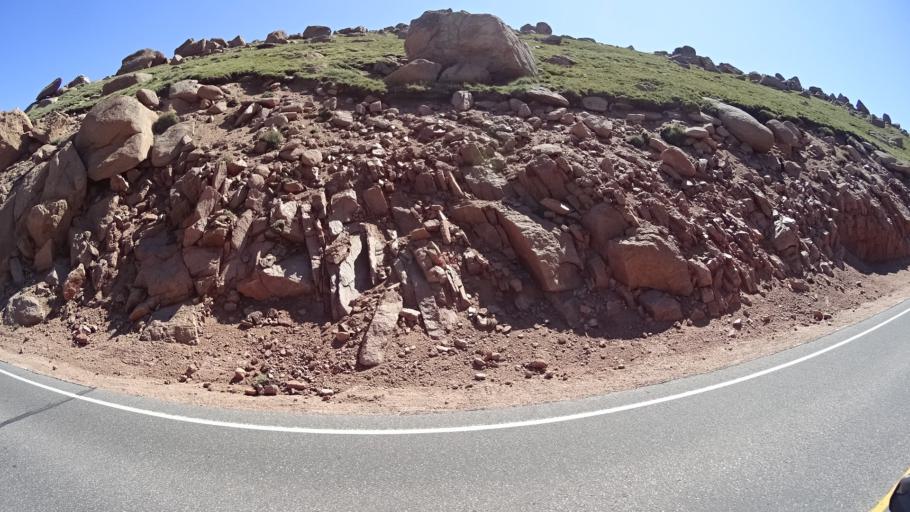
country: US
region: Colorado
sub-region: El Paso County
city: Cascade-Chipita Park
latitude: 38.8727
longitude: -105.0678
